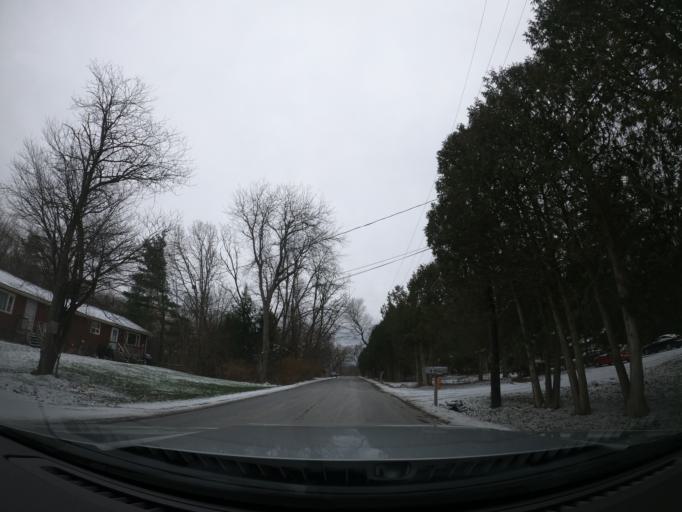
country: US
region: New York
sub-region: Tompkins County
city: Northeast Ithaca
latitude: 42.4693
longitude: -76.4502
